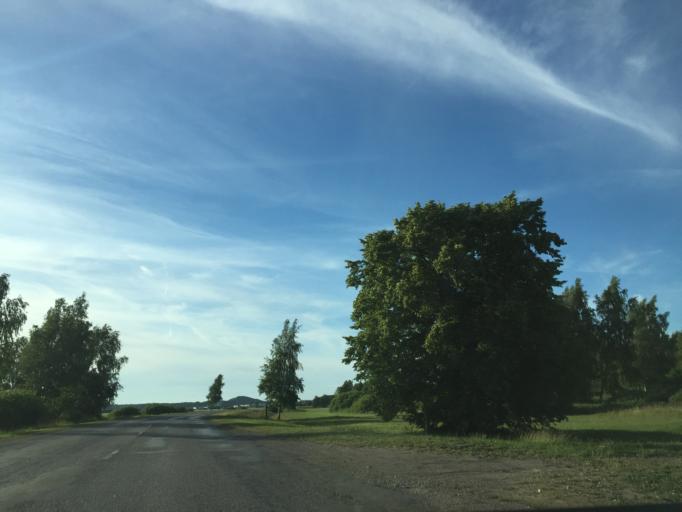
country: LV
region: Ventspils
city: Ventspils
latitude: 57.3477
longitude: 21.5666
